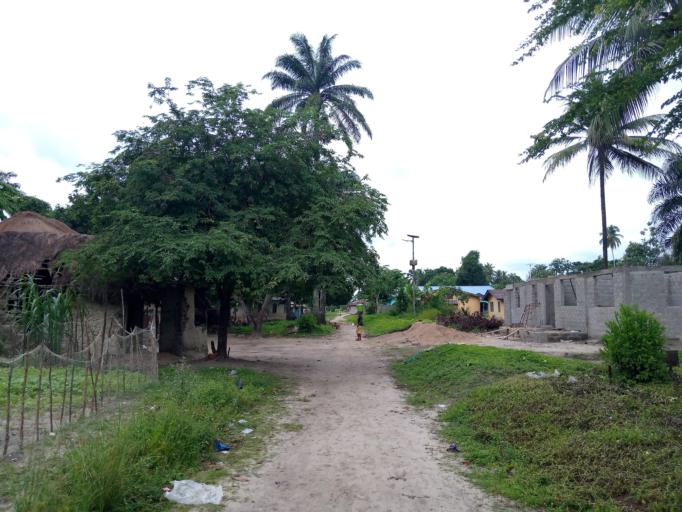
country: SL
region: Southern Province
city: Bonthe
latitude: 7.5302
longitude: -12.5081
